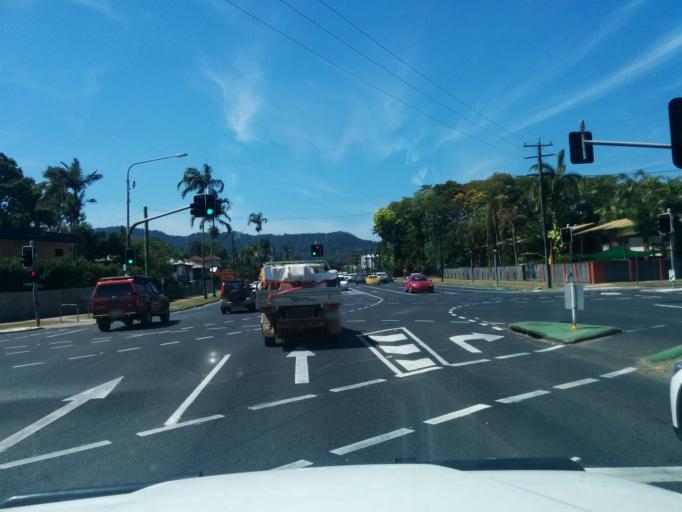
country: AU
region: Queensland
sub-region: Cairns
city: Cairns
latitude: -16.9230
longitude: 145.7400
